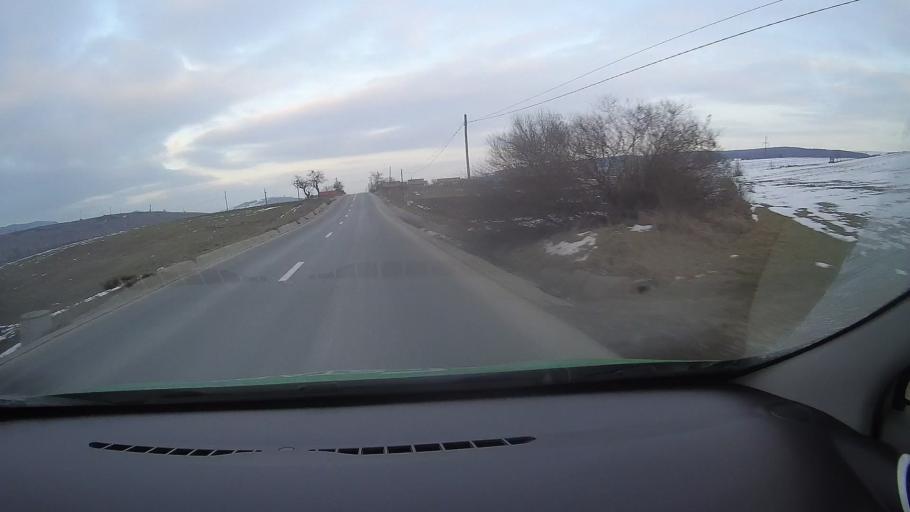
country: RO
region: Harghita
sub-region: Comuna Lupeni
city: Lupeni
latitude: 46.3565
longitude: 25.2102
